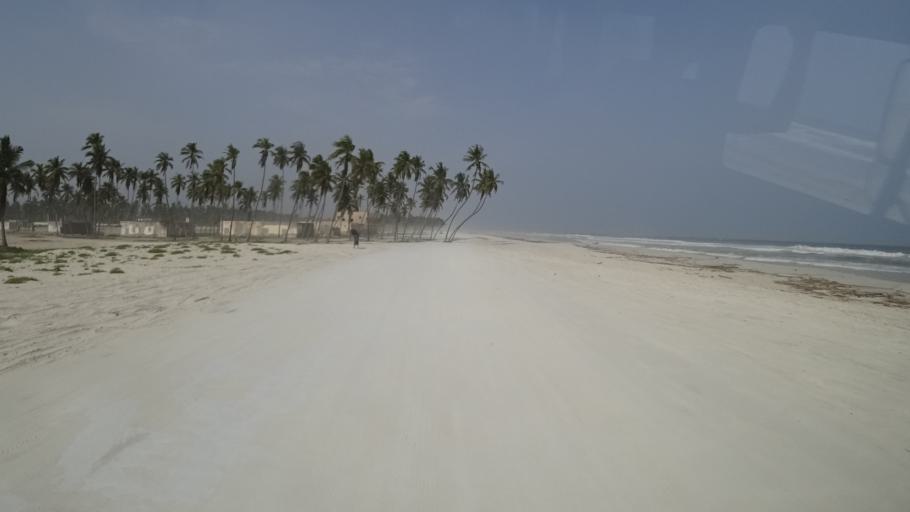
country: OM
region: Zufar
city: Salalah
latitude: 17.0009
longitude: 54.1101
